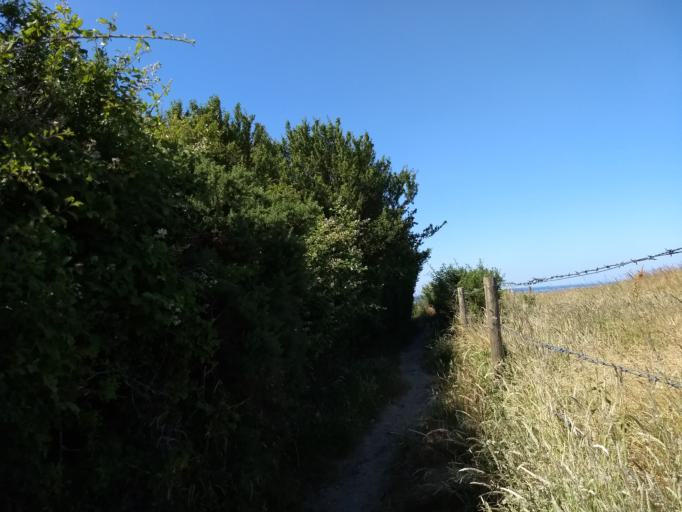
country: GB
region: England
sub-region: Isle of Wight
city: Gurnard
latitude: 50.7467
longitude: -1.3432
